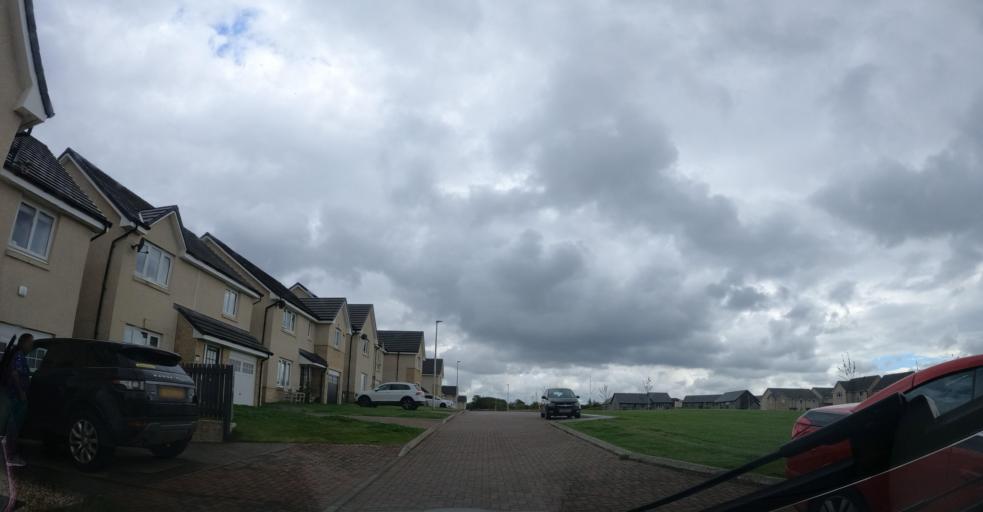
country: GB
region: Scotland
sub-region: West Lothian
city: West Calder
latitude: 55.8570
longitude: -3.5756
